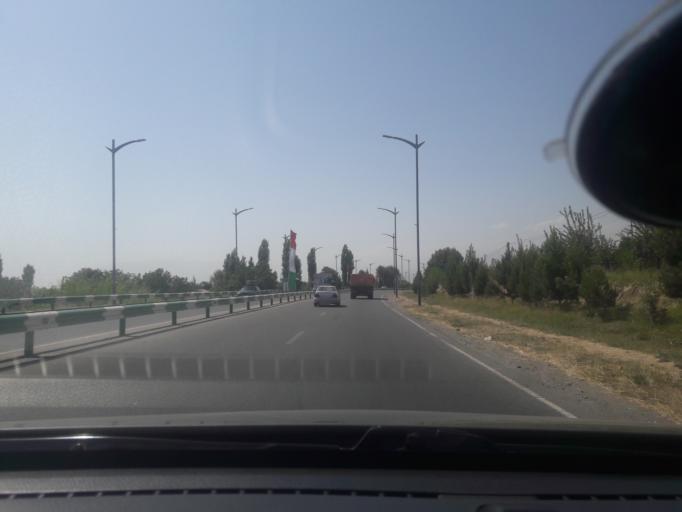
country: TJ
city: Shahrinav
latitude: 38.5644
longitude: 68.3946
